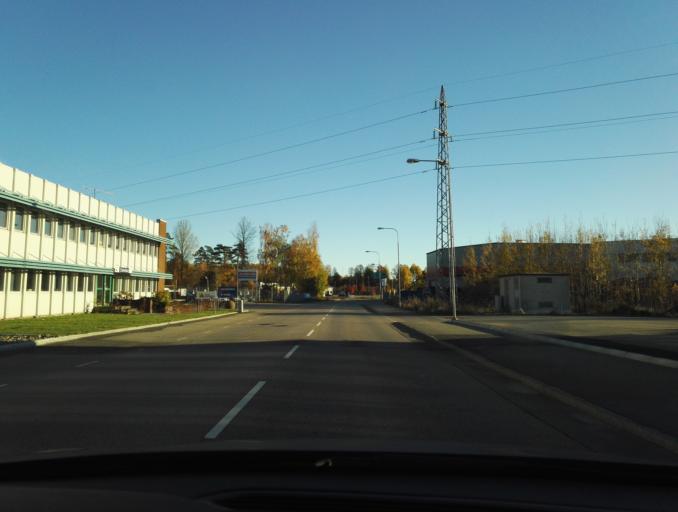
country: SE
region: Kronoberg
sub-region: Vaxjo Kommun
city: Vaexjoe
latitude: 56.8937
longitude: 14.7761
